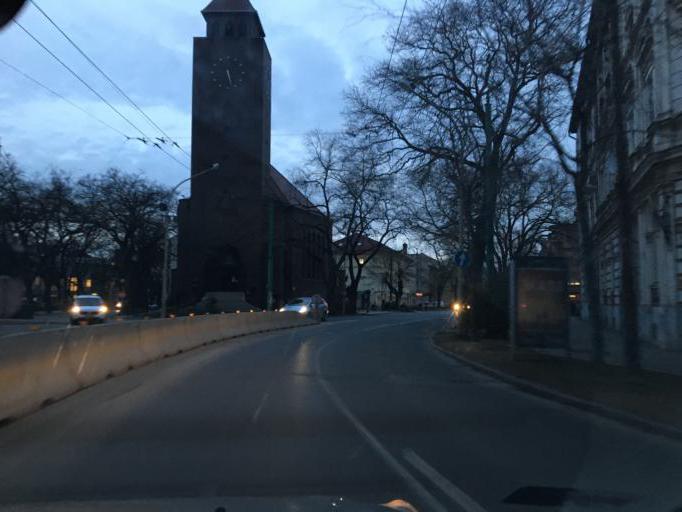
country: HU
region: Csongrad
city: Szeged
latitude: 46.2483
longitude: 20.1454
